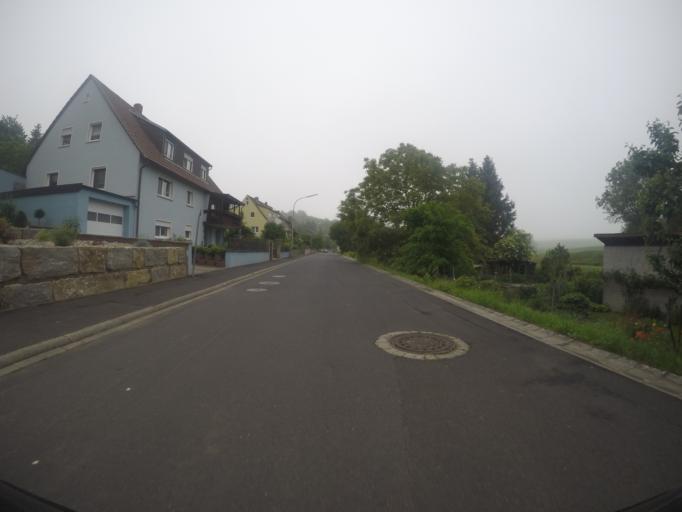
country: DE
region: Bavaria
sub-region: Regierungsbezirk Unterfranken
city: Schwanfeld
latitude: 49.9211
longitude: 10.1468
